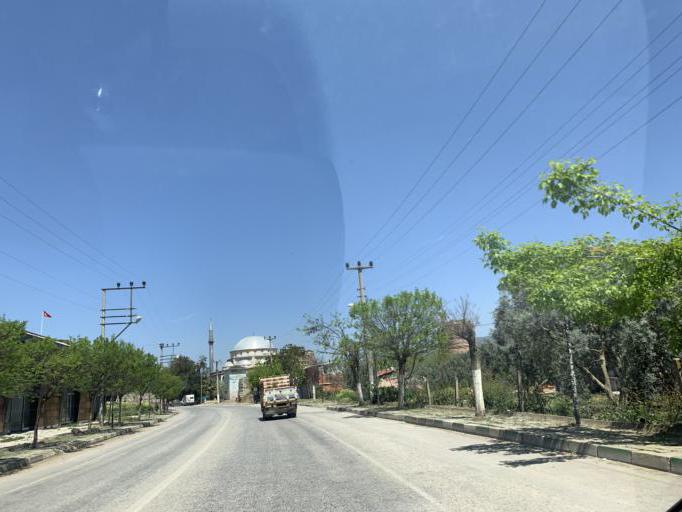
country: TR
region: Bursa
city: Iznik
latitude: 40.4224
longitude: 29.7197
